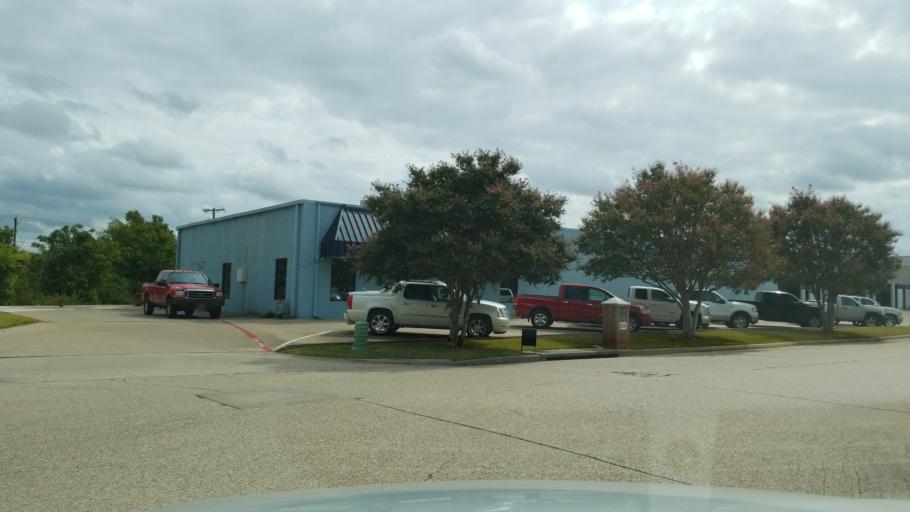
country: US
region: Texas
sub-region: Dallas County
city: Garland
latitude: 32.8915
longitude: -96.6815
